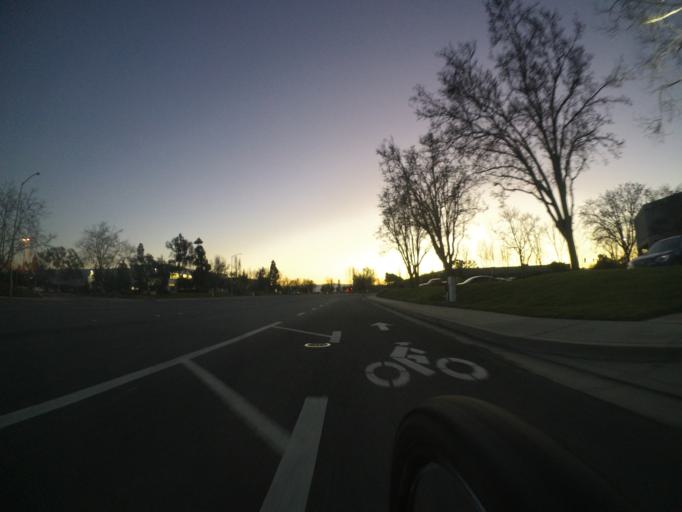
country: US
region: California
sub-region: Santa Clara County
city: Milpitas
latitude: 37.4751
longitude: -121.9394
